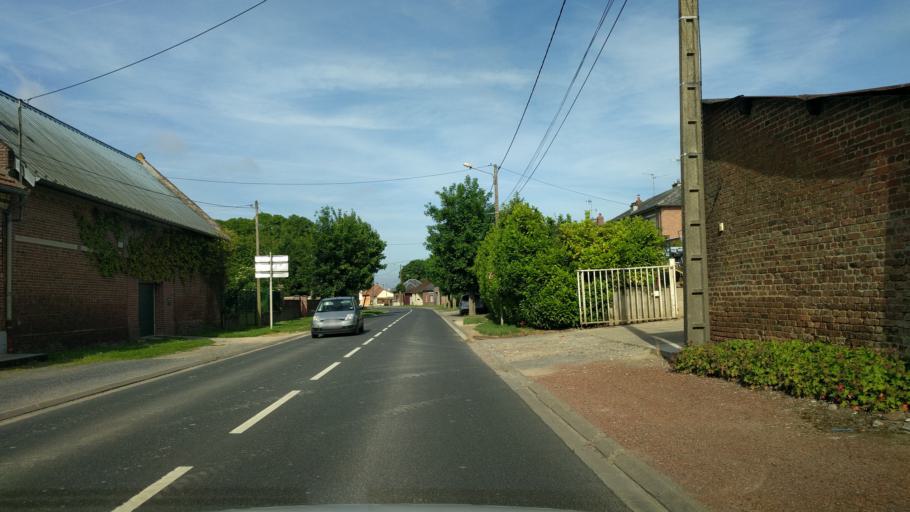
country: FR
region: Picardie
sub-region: Departement de la Somme
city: Peronne
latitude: 49.9585
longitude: 2.8860
